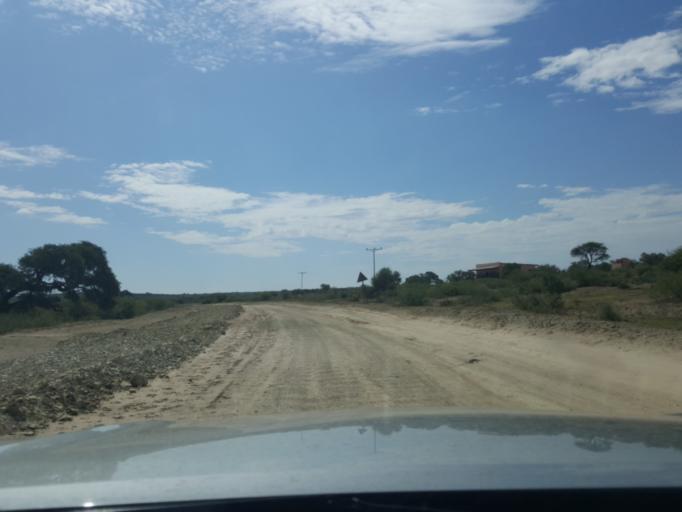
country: BW
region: Kweneng
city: Letlhakeng
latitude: -23.9872
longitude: 24.9708
